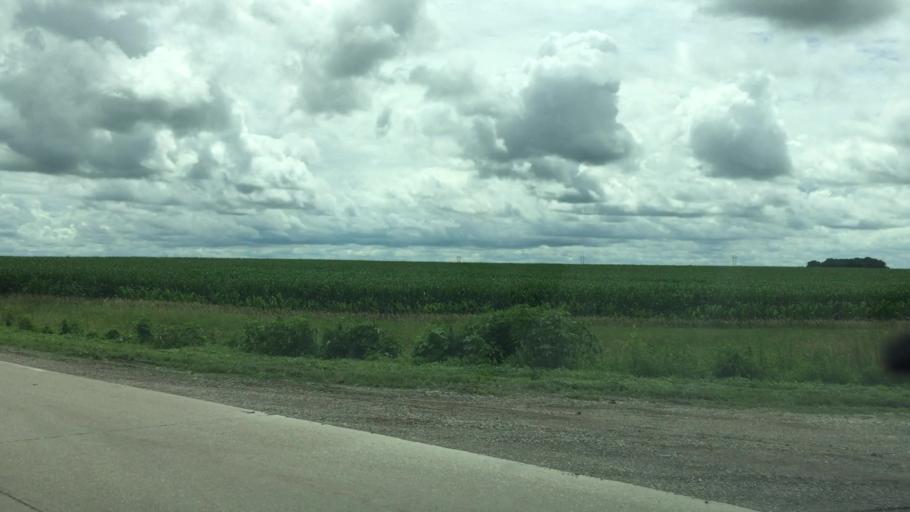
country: US
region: Iowa
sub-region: Jasper County
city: Prairie City
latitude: 41.5807
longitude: -93.1595
